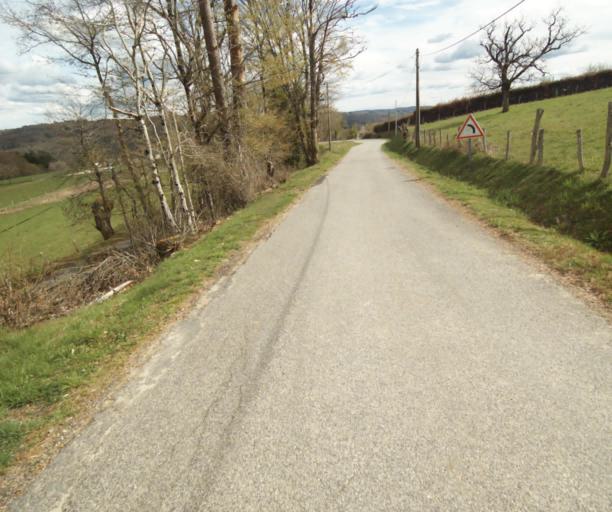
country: FR
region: Limousin
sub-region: Departement de la Correze
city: Argentat
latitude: 45.1800
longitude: 1.9451
